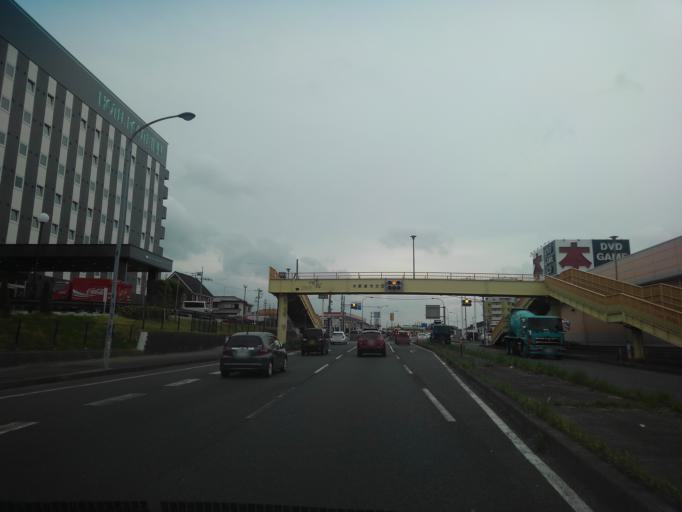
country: JP
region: Chiba
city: Kisarazu
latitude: 35.3822
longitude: 139.9423
